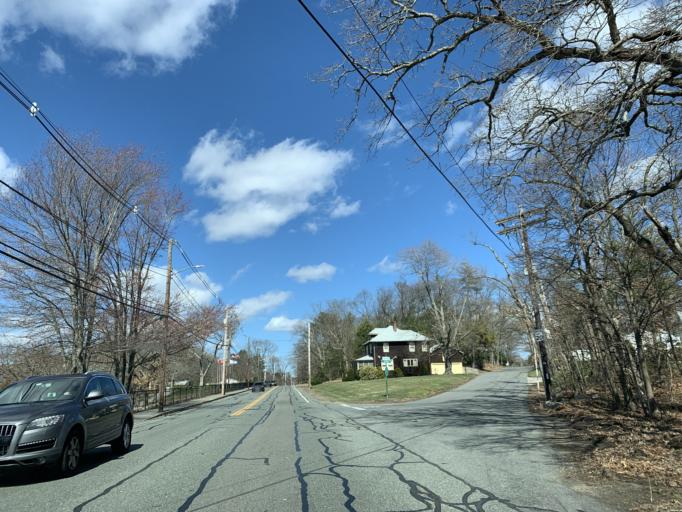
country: US
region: Massachusetts
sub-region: Norfolk County
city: Canton
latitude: 42.1786
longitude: -71.1295
